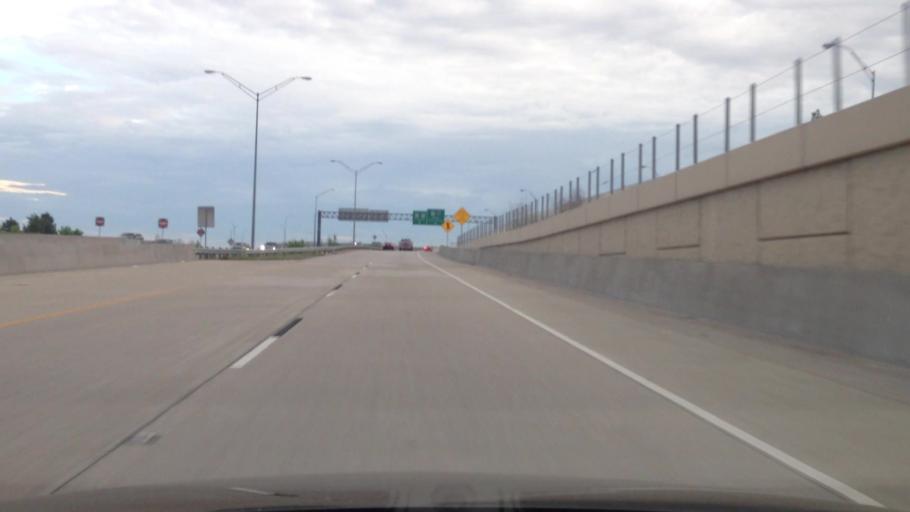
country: US
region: Texas
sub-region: Dallas County
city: Coppell
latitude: 32.9688
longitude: -97.0371
